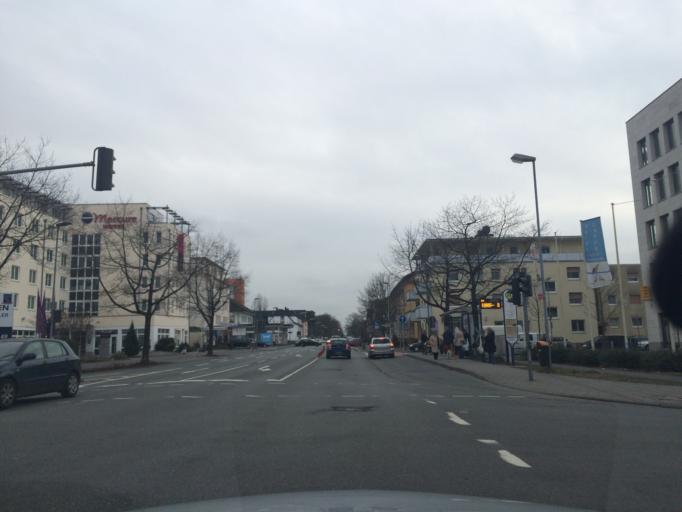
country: DE
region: Hesse
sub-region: Regierungsbezirk Darmstadt
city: Neu Isenburg
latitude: 50.0482
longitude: 8.6952
